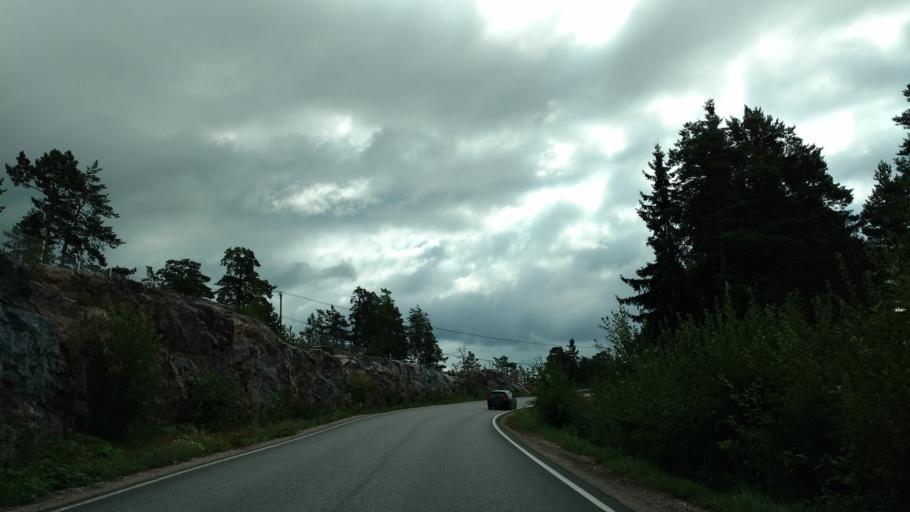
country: FI
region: Varsinais-Suomi
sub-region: Aboland-Turunmaa
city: Dragsfjaerd
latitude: 59.9876
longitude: 22.4537
